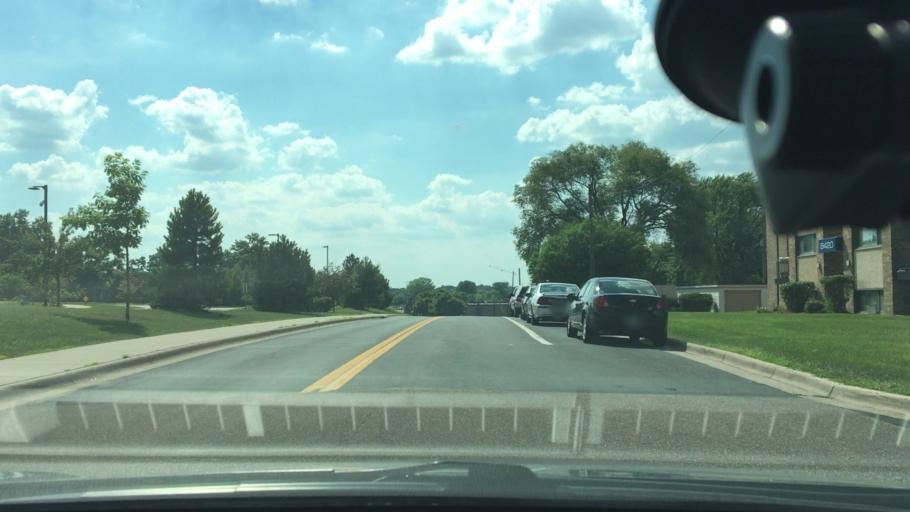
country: US
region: Minnesota
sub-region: Hennepin County
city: New Hope
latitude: 45.0548
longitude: -93.3863
